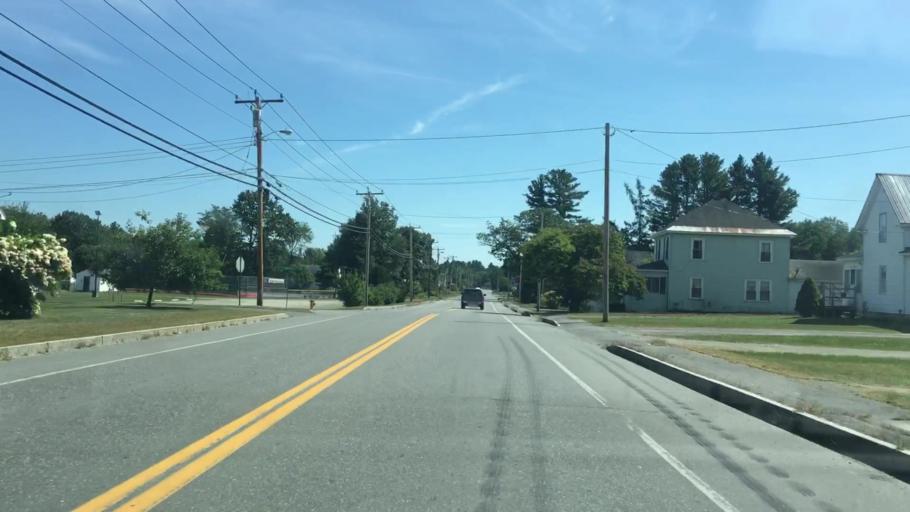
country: US
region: Maine
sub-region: Piscataquis County
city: Milo
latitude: 45.2476
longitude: -68.9787
